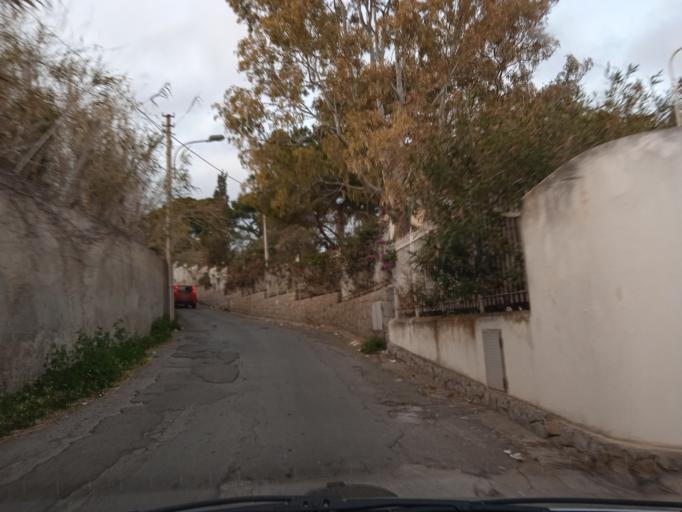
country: IT
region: Sicily
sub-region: Palermo
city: Santa Flavia
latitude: 38.0932
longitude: 13.5397
